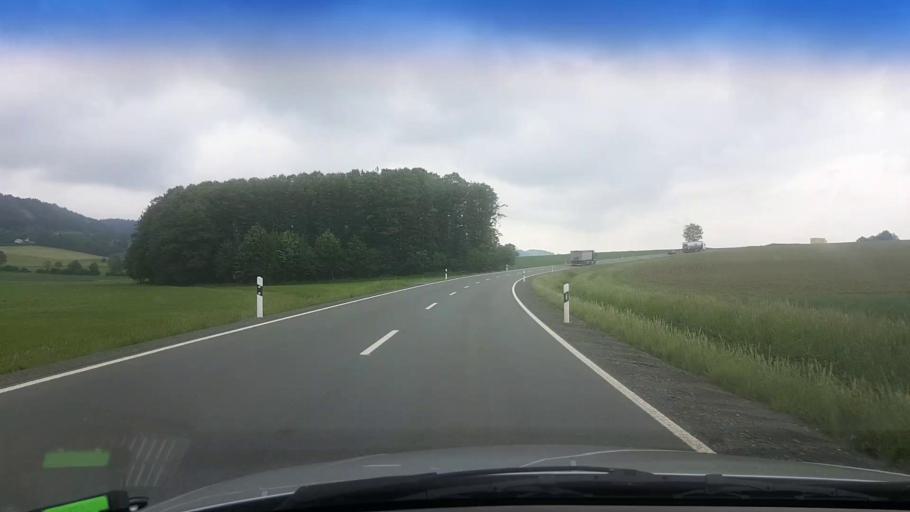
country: DE
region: Bavaria
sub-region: Upper Franconia
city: Gesees
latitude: 50.0236
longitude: 11.6631
